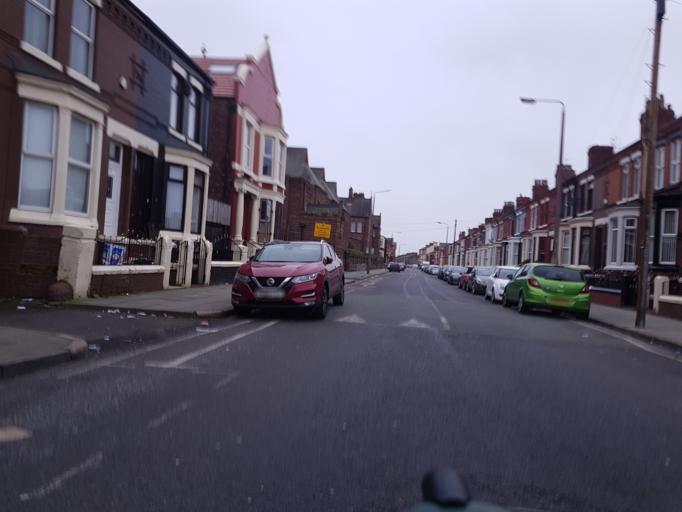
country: GB
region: England
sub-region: Liverpool
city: Liverpool
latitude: 53.4431
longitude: -2.9726
